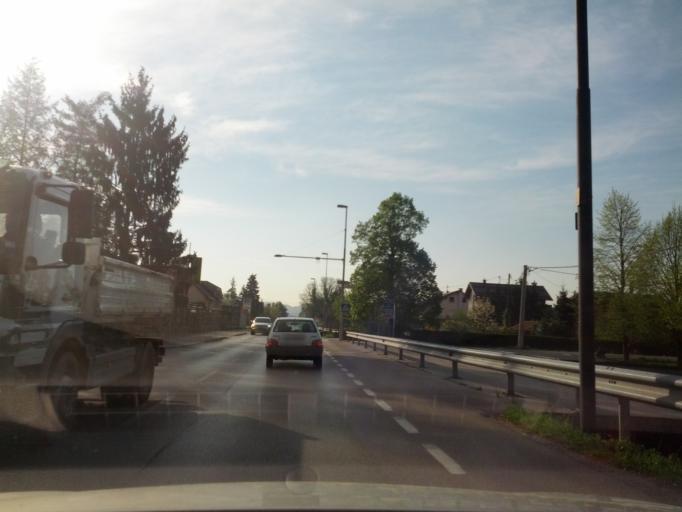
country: SI
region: Ljubljana
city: Ljubljana
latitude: 46.0288
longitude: 14.5226
